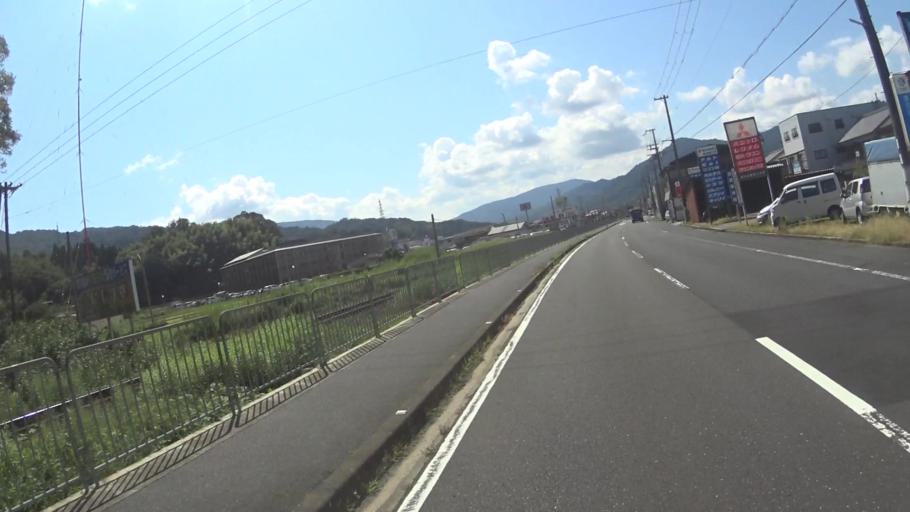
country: JP
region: Kyoto
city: Miyazu
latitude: 35.5396
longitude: 135.2074
